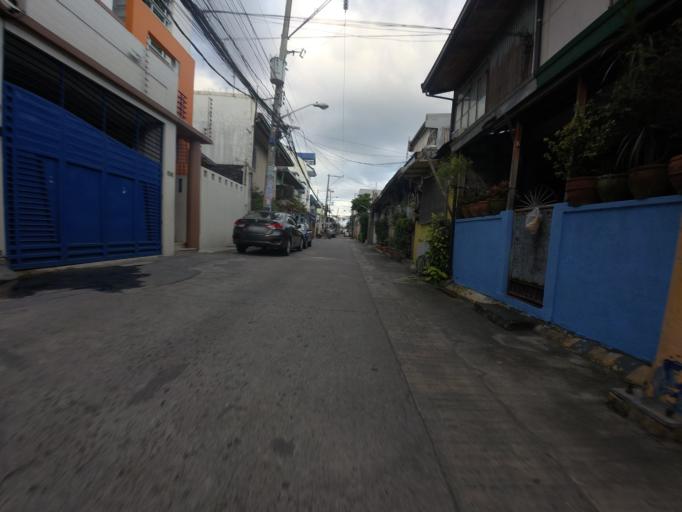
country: PH
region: Metro Manila
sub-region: Mandaluyong
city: Mandaluyong City
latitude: 14.5761
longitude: 121.0147
